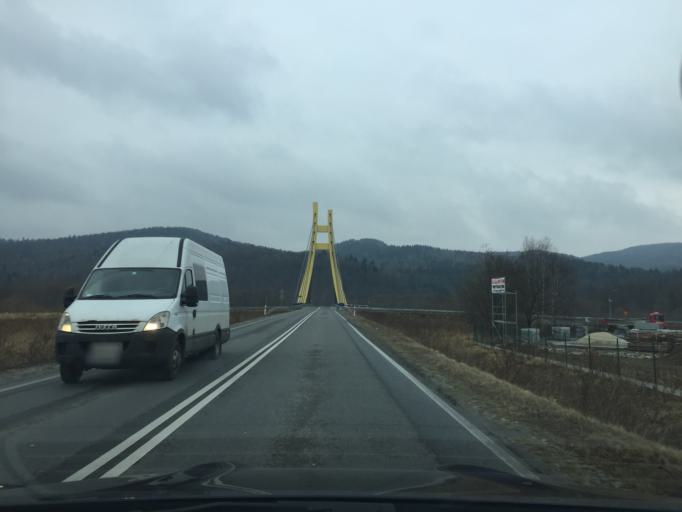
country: PL
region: Lesser Poland Voivodeship
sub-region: Powiat suski
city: Zembrzyce
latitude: 49.7687
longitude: 19.6003
